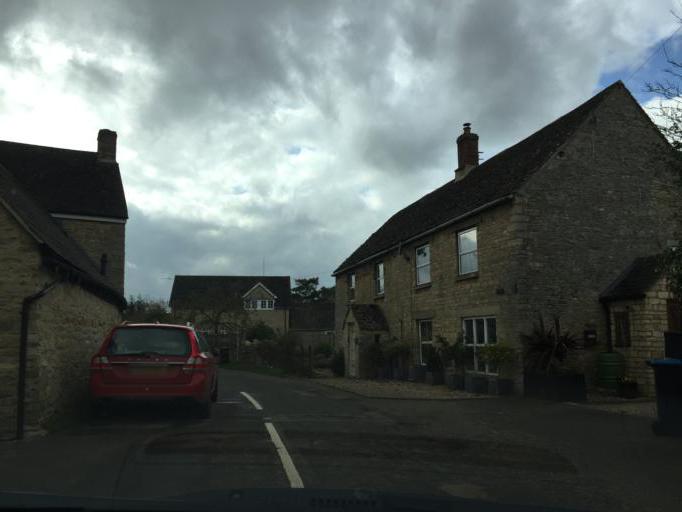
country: GB
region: England
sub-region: Oxfordshire
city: Stonesfield
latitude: 51.8520
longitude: -1.4290
